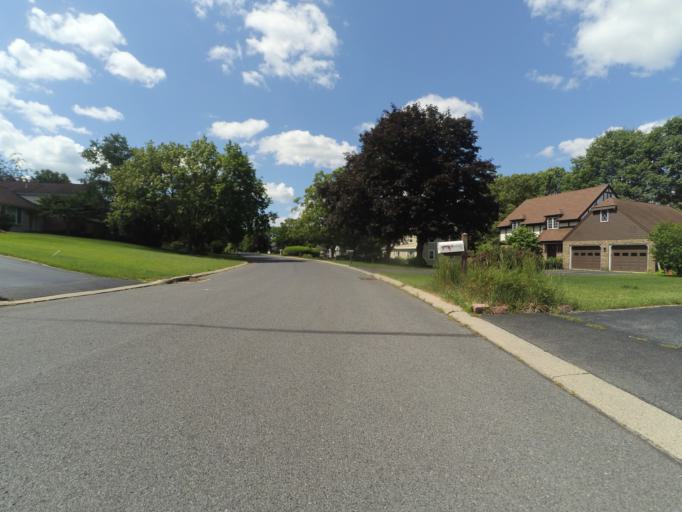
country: US
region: Pennsylvania
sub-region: Centre County
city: Lemont
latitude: 40.7962
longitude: -77.8264
